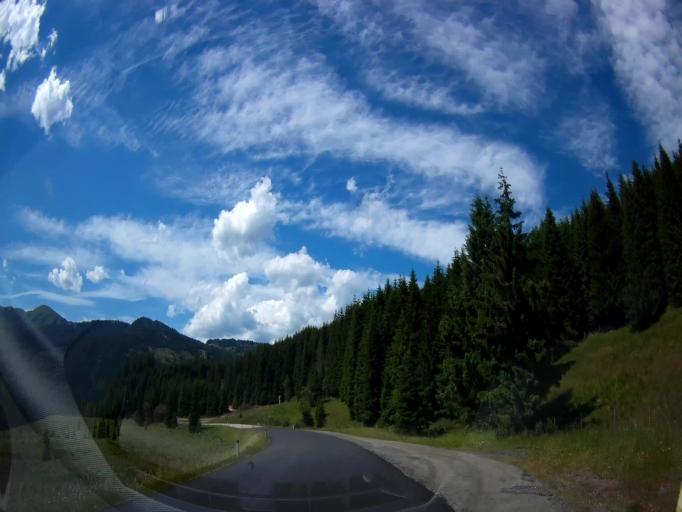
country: AT
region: Styria
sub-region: Politischer Bezirk Murau
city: Stadl an der Mur
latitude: 46.9706
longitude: 14.0163
